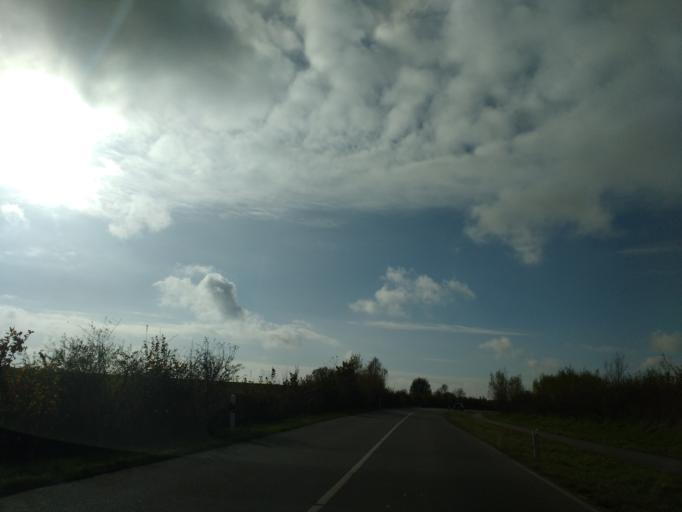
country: DE
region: Mecklenburg-Vorpommern
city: Ostseebad Boltenhagen
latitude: 53.9687
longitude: 11.2339
